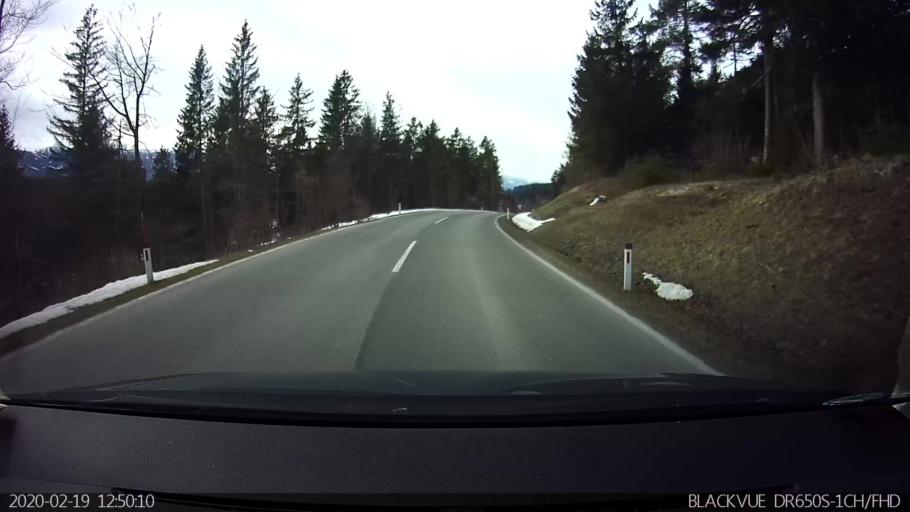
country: AT
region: Tyrol
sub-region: Politischer Bezirk Innsbruck Land
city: Gnadenwald
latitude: 47.3176
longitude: 11.5502
